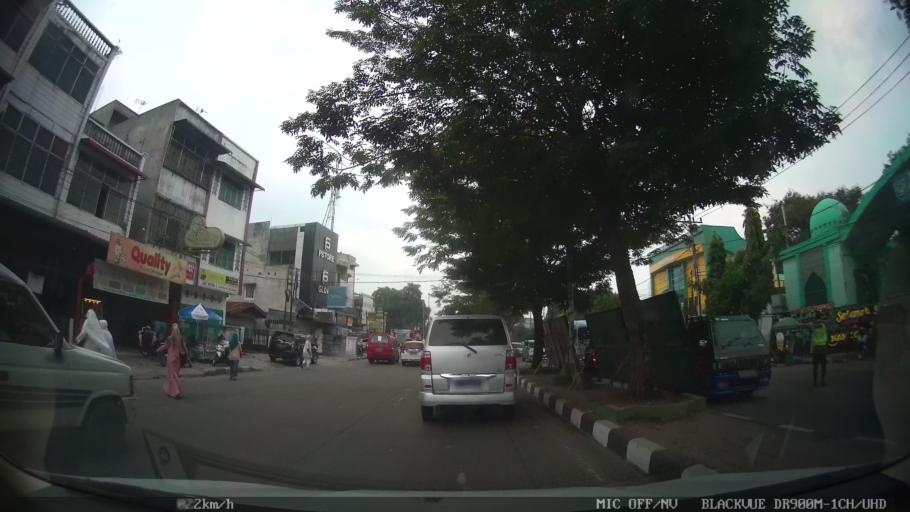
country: ID
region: North Sumatra
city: Medan
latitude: 3.5620
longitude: 98.6932
